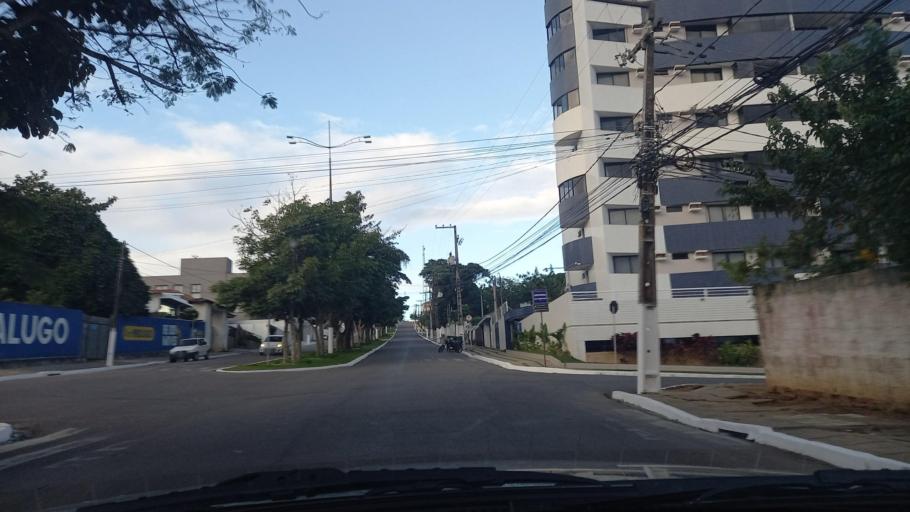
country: BR
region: Pernambuco
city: Garanhuns
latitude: -8.8809
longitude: -36.4748
